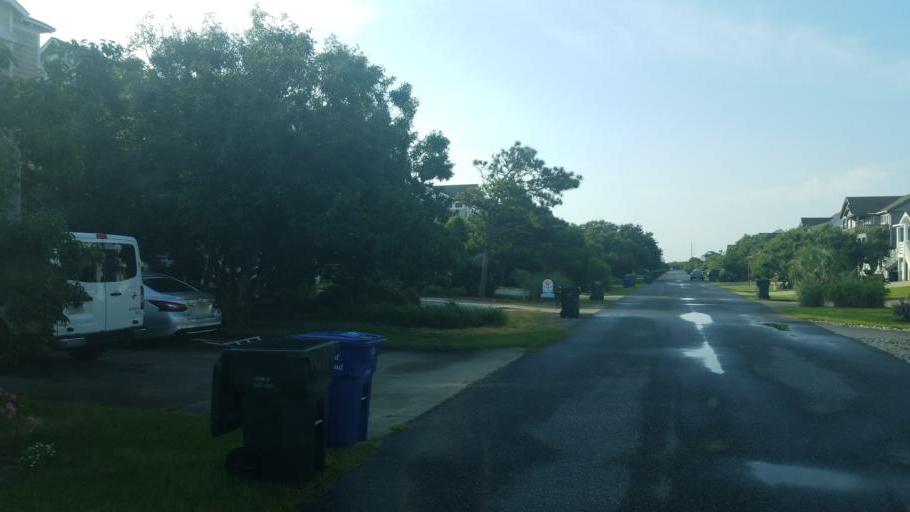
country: US
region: North Carolina
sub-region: Dare County
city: Nags Head
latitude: 35.9727
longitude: -75.6344
